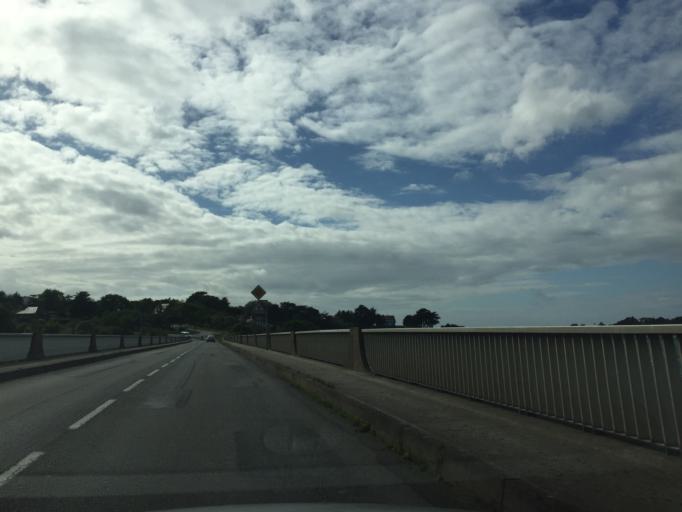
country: FR
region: Brittany
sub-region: Departement d'Ille-et-Vilaine
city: Saint-Briac-sur-Mer
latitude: 48.6163
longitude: -2.1392
